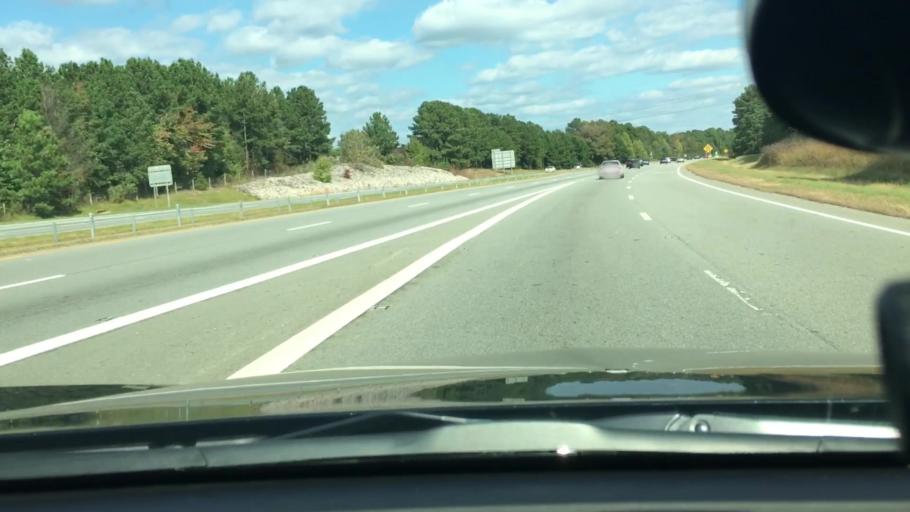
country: US
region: North Carolina
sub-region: Wake County
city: Apex
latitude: 35.7162
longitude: -78.8384
